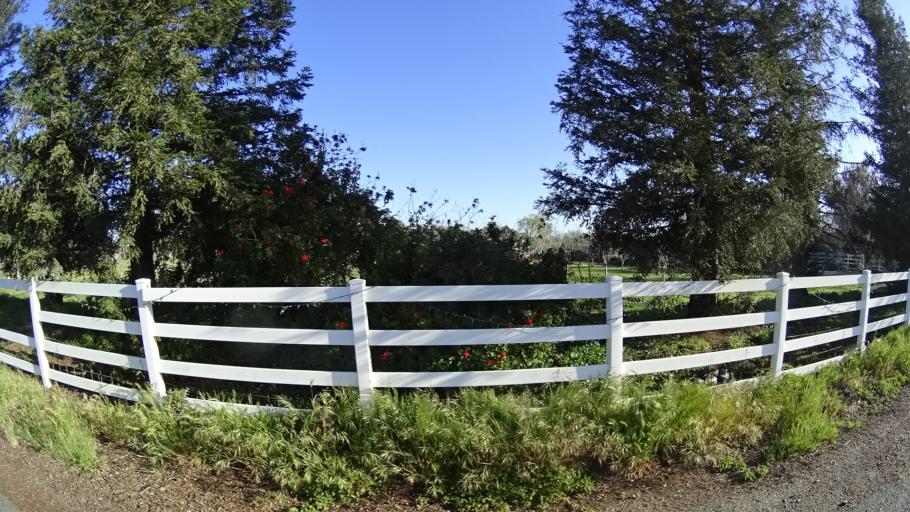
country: US
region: California
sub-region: Glenn County
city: Orland
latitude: 39.7694
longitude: -122.2181
